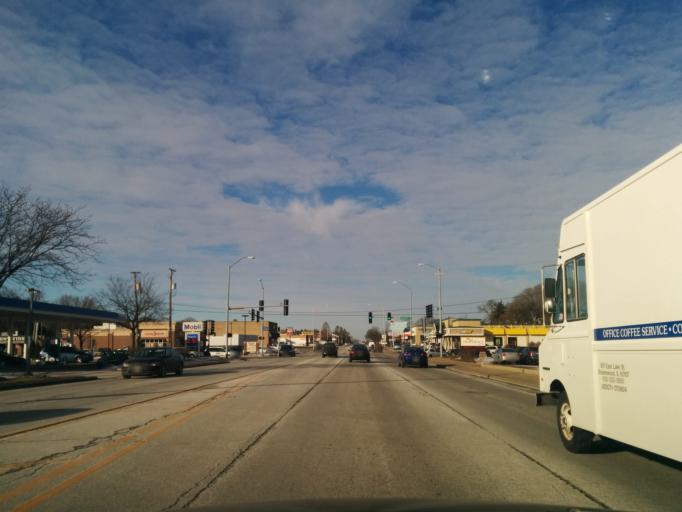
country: US
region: Illinois
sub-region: DuPage County
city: Wheaton
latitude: 41.8591
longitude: -88.0909
